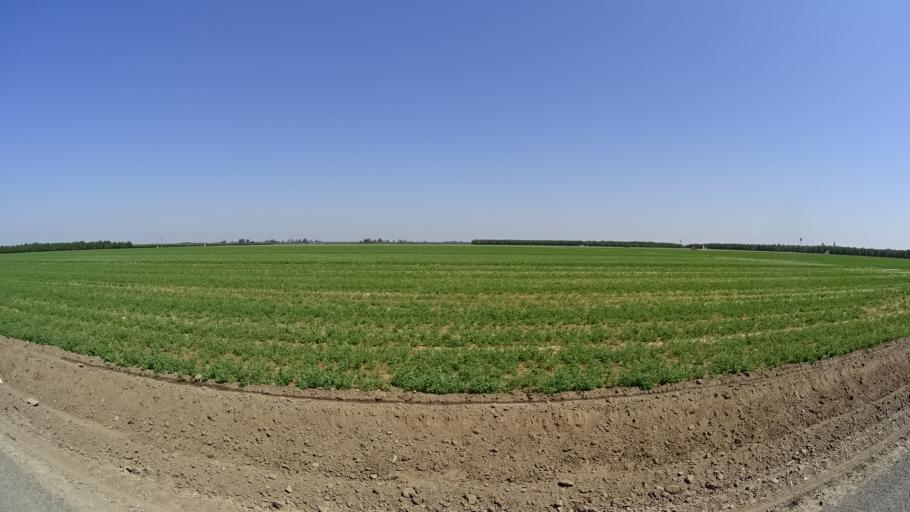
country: US
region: California
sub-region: Kings County
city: Lucerne
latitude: 36.3719
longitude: -119.6891
